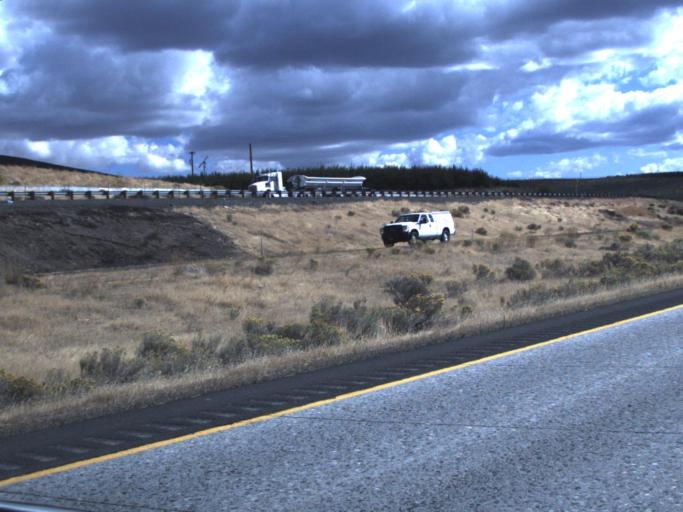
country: US
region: Washington
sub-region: Yakima County
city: Union Gap
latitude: 46.5150
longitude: -120.4549
